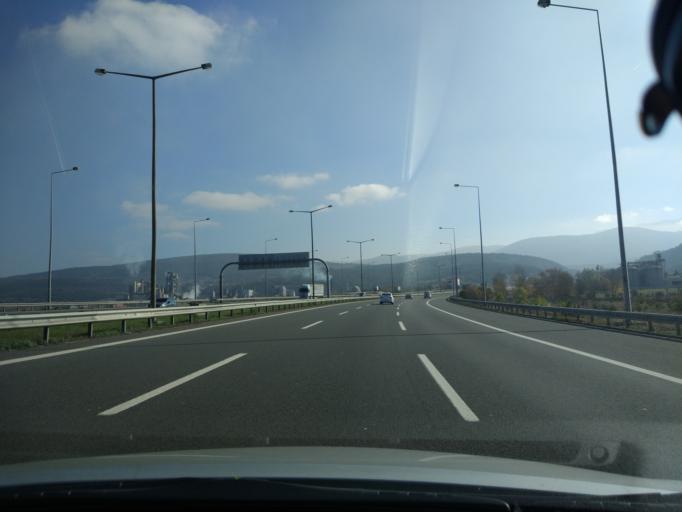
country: TR
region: Bolu
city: Bolu
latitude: 40.7595
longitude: 31.7690
